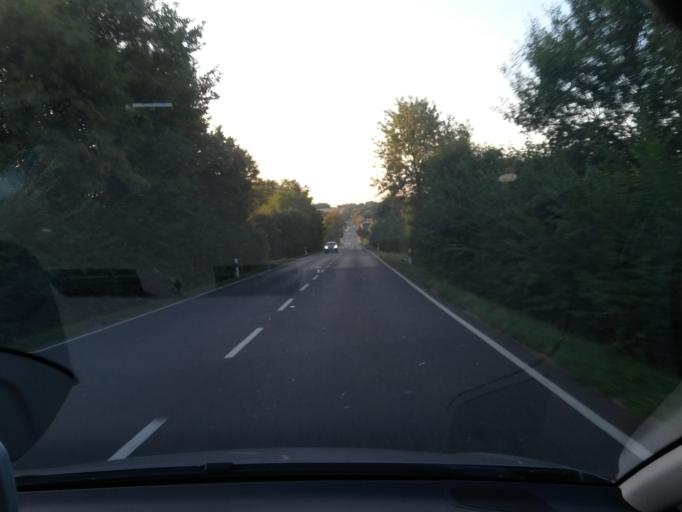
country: LU
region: Luxembourg
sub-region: Canton d'Esch-sur-Alzette
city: Frisange
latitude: 49.5293
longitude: 6.1819
